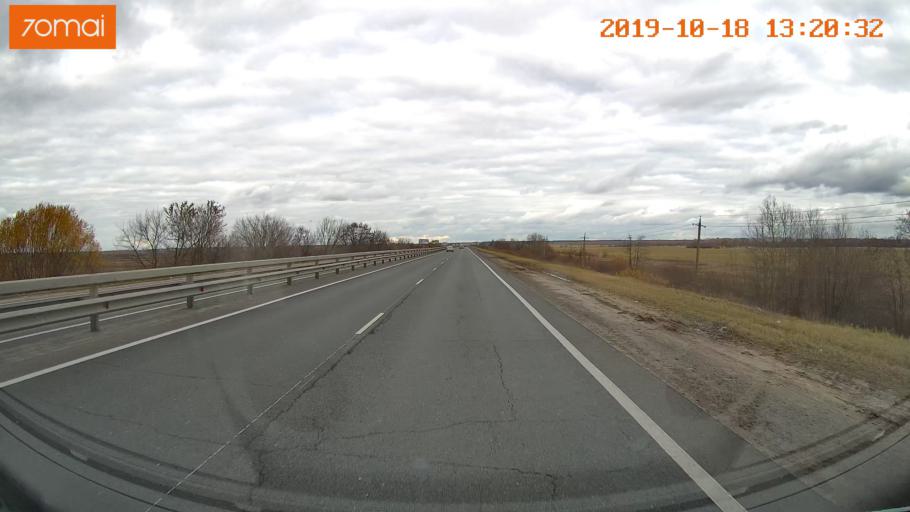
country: RU
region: Rjazan
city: Polyany
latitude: 54.6789
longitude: 39.8302
